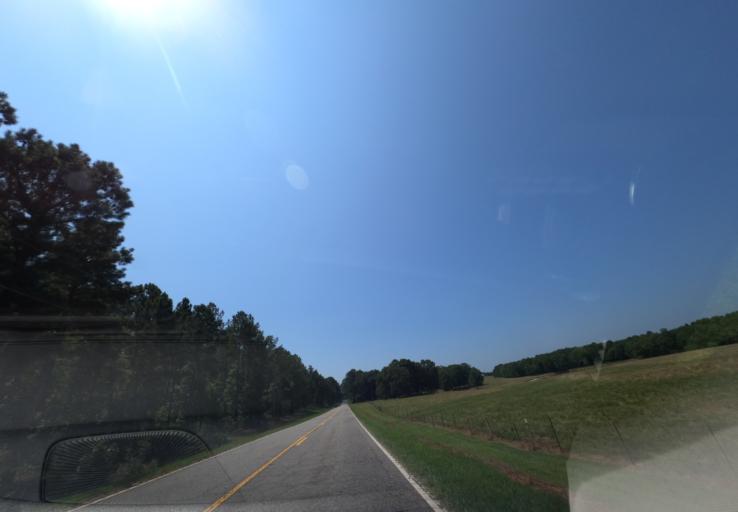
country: US
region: South Carolina
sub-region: McCormick County
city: McCormick
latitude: 33.9867
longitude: -82.1299
